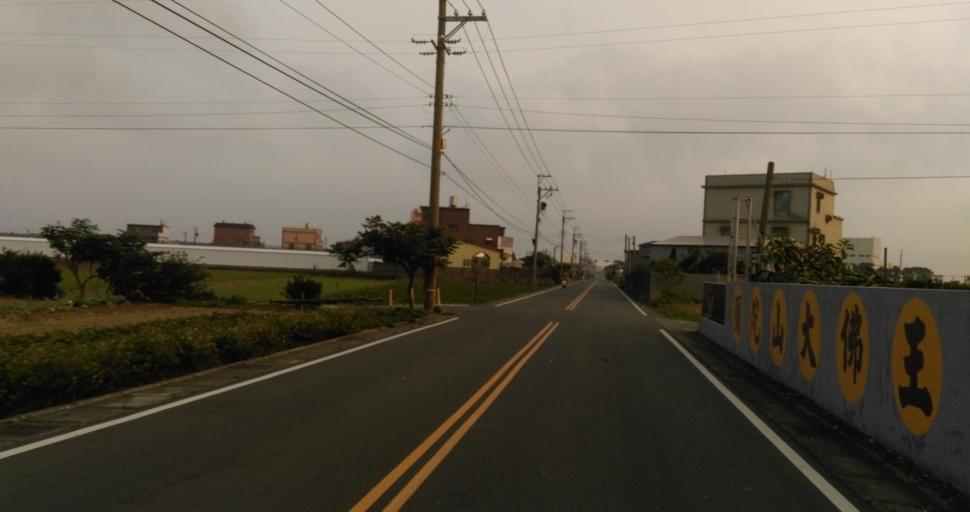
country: TW
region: Taiwan
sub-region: Hsinchu
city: Zhubei
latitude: 24.8677
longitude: 120.9589
